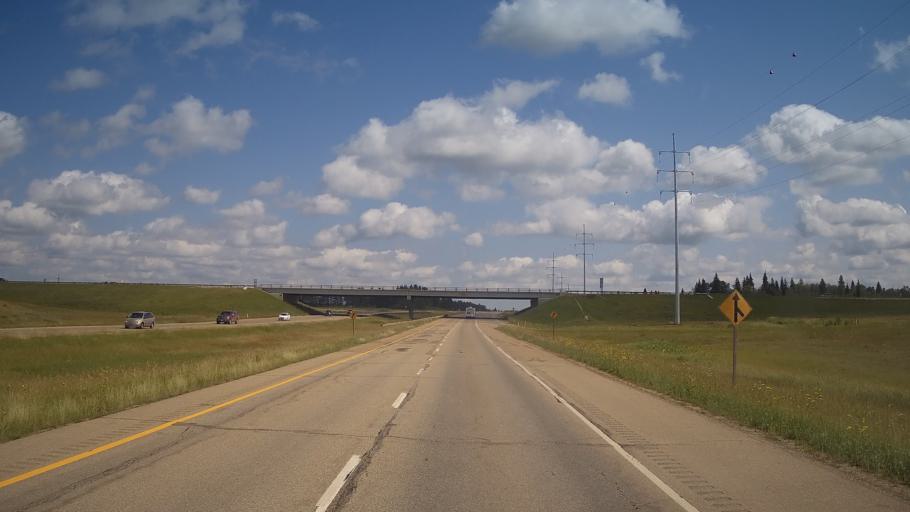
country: CA
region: Alberta
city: Sherwood Park
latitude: 53.4467
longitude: -113.2496
